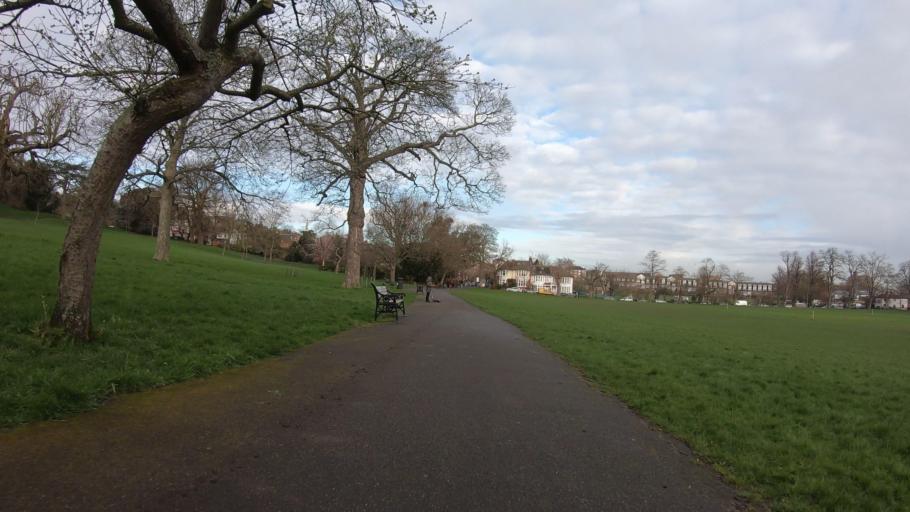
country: GB
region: England
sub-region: Greater London
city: Hackney
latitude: 51.5662
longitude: -0.0483
